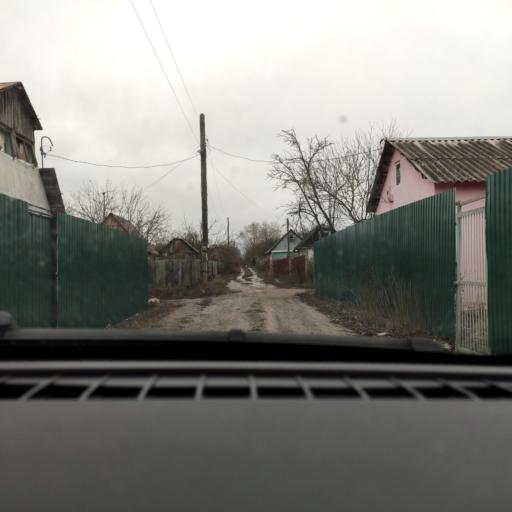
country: RU
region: Voronezj
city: Maslovka
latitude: 51.6102
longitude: 39.2759
